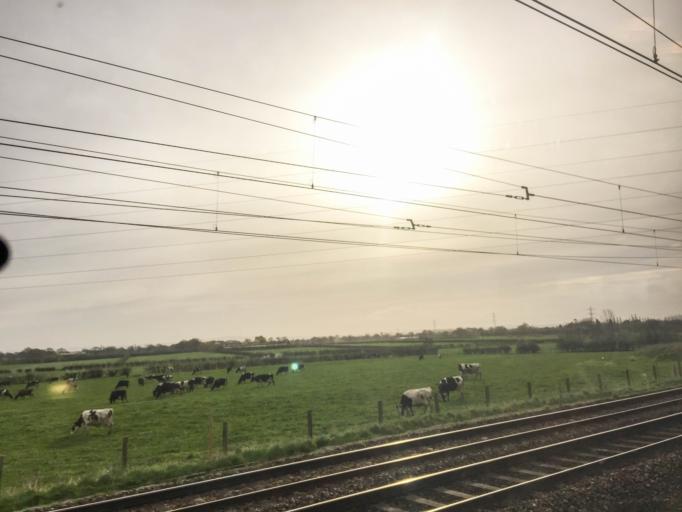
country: GB
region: England
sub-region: Cheshire East
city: Crewe
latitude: 53.1335
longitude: -2.4589
